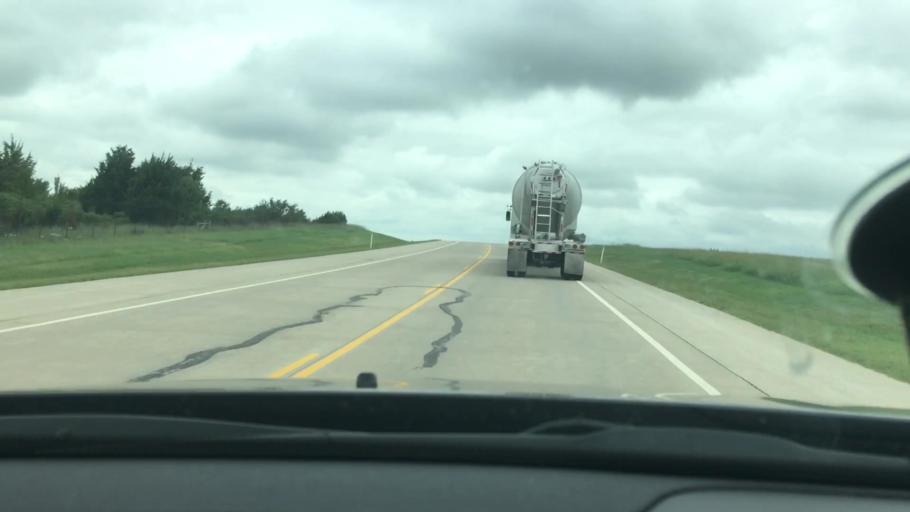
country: US
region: Oklahoma
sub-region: Murray County
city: Sulphur
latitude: 34.5851
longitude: -96.9136
